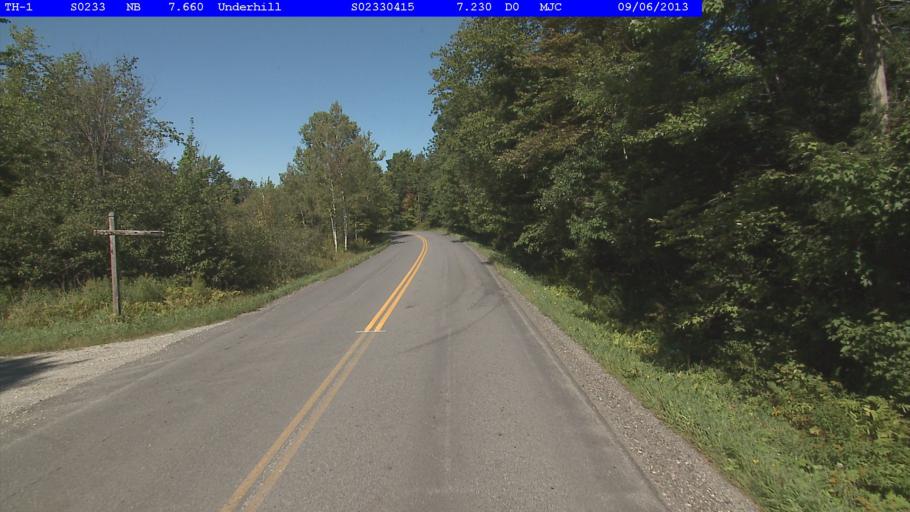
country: US
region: Vermont
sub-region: Chittenden County
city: Jericho
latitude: 44.5689
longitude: -72.8644
